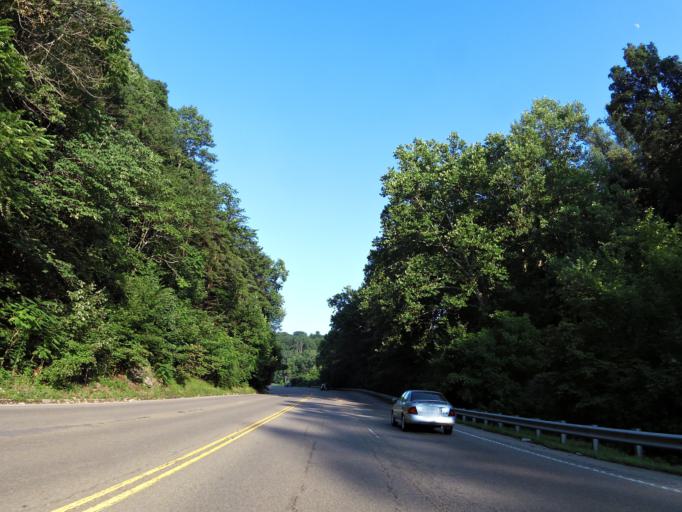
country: US
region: Tennessee
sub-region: Anderson County
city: Clinton
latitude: 36.0266
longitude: -84.0829
